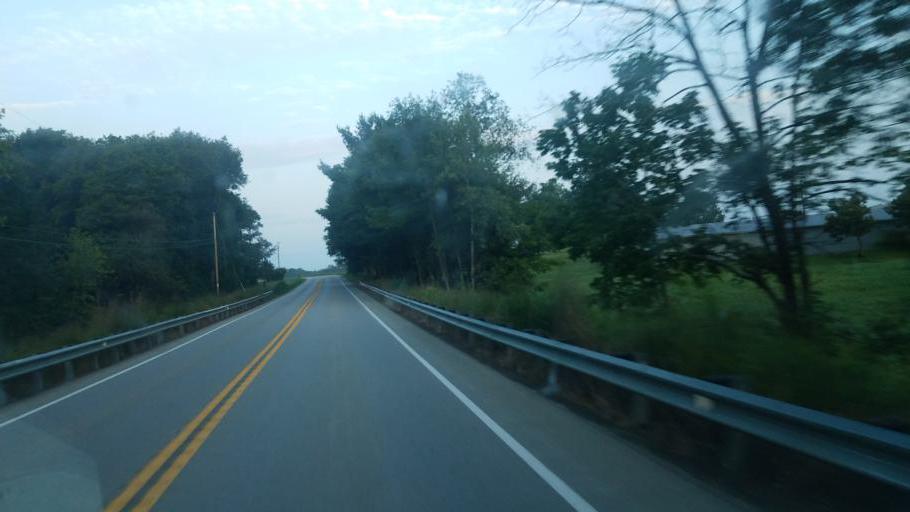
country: US
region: Pennsylvania
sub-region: Crawford County
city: Conneaut Lakeshore
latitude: 41.5702
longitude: -80.2690
